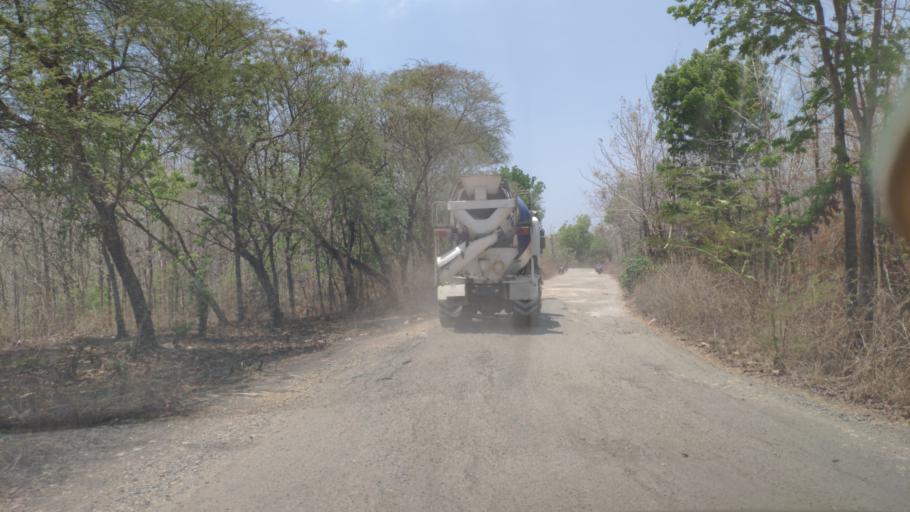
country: ID
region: Central Java
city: Randublatung
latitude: -7.2390
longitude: 111.3796
